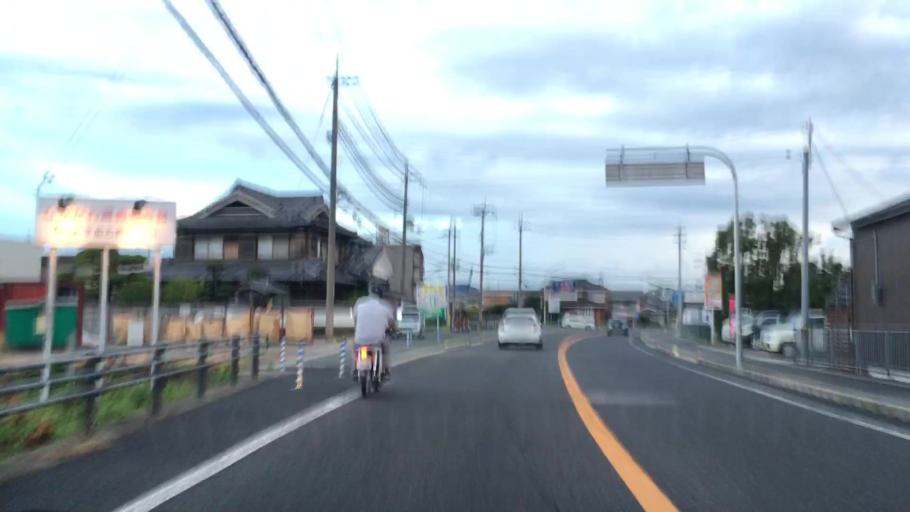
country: JP
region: Hyogo
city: Himeji
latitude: 34.9118
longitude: 134.7391
